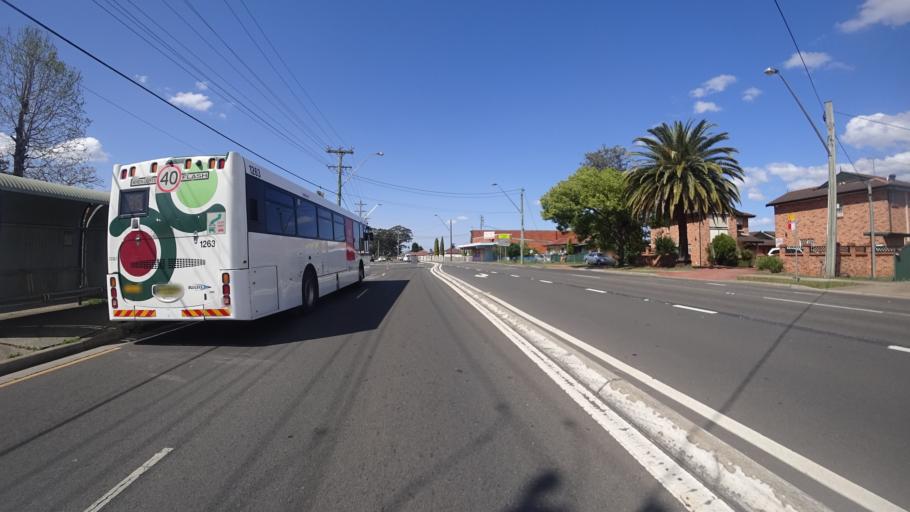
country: AU
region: New South Wales
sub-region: Fairfield
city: Cabramatta West
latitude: -33.8994
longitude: 150.9202
